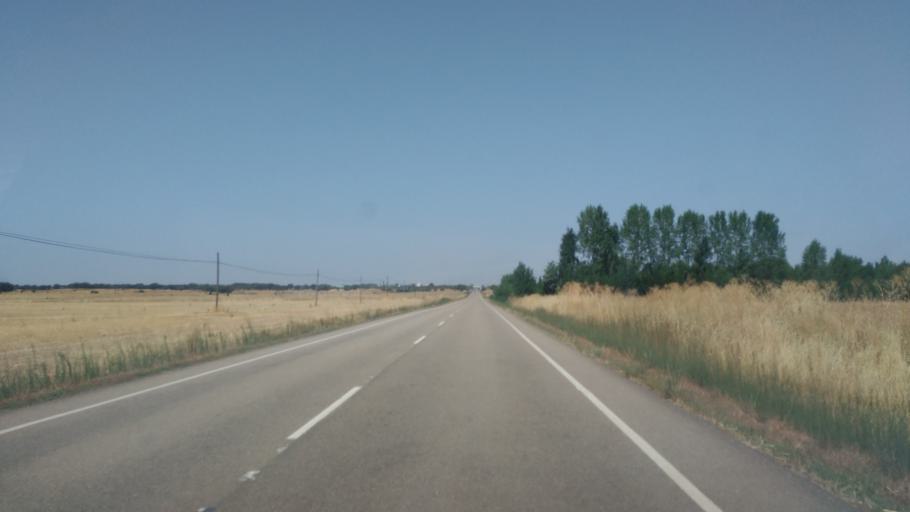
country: ES
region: Castille and Leon
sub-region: Provincia de Salamanca
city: La Fuente de San Esteban
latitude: 40.7784
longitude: -6.2311
